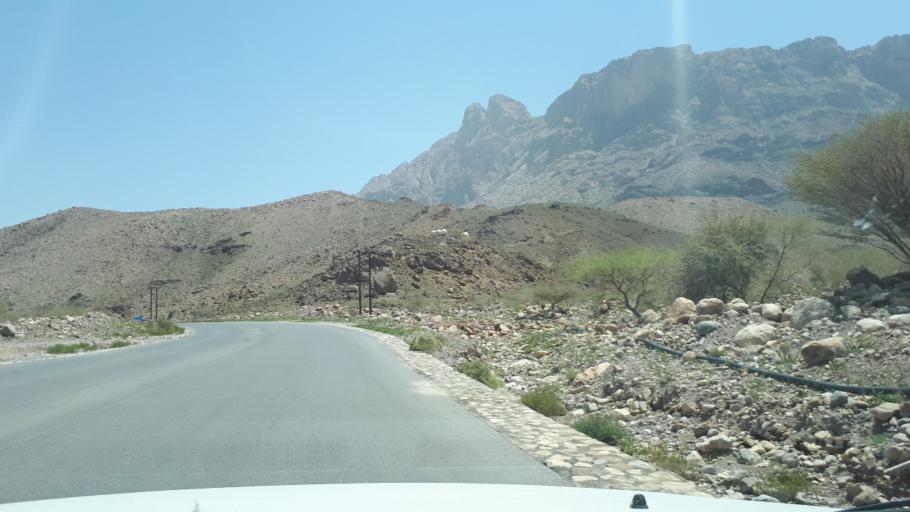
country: OM
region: Muhafazat ad Dakhiliyah
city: Bahla'
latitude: 23.1552
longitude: 57.1791
